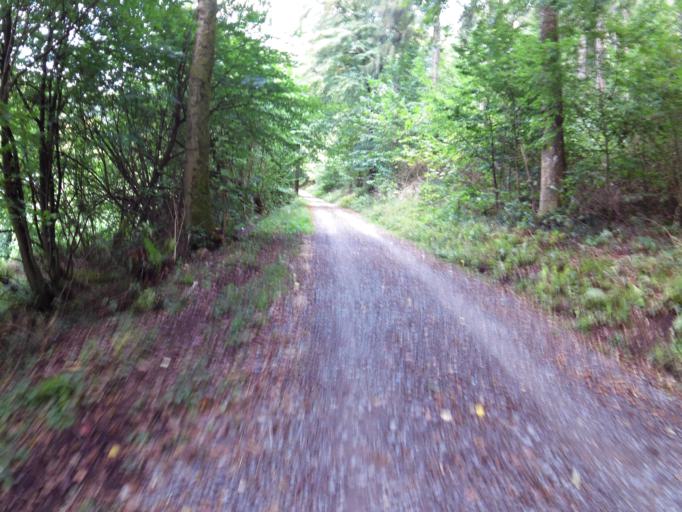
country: DE
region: Baden-Wuerttemberg
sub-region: Karlsruhe Region
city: Zwingenberg
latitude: 49.4145
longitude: 9.0164
